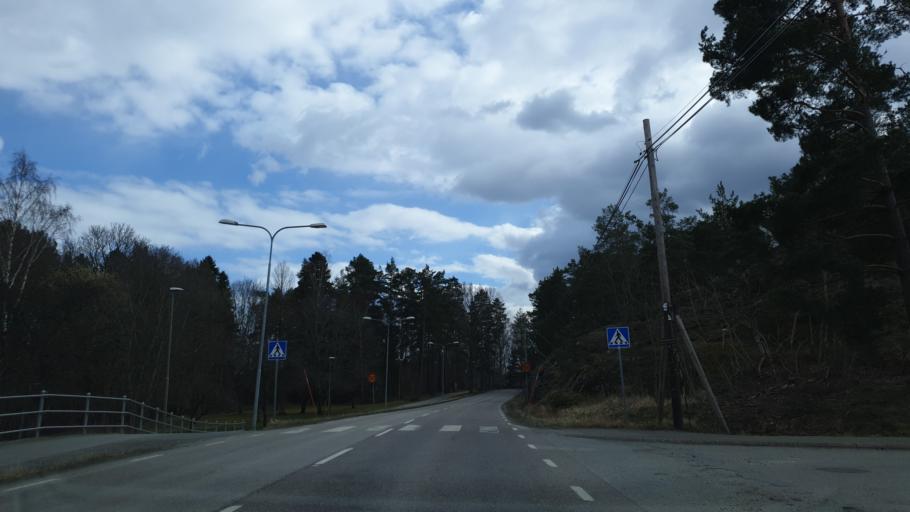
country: SE
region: Stockholm
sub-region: Varmdo Kommun
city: Mortnas
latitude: 59.2808
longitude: 18.4262
